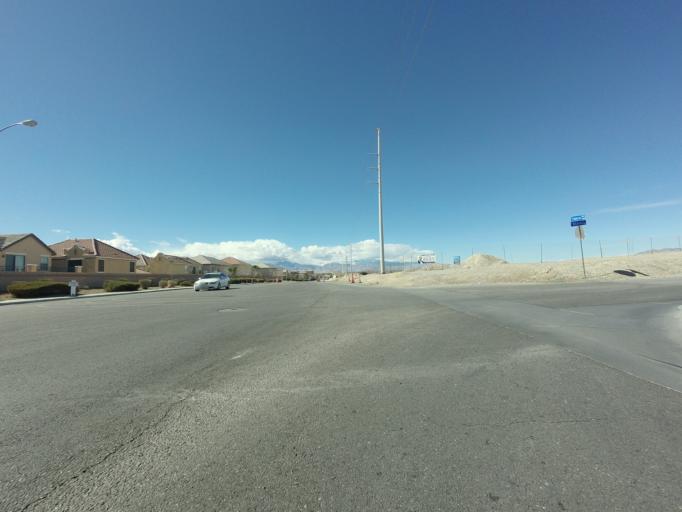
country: US
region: Nevada
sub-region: Clark County
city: Nellis Air Force Base
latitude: 36.2691
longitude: -115.1123
